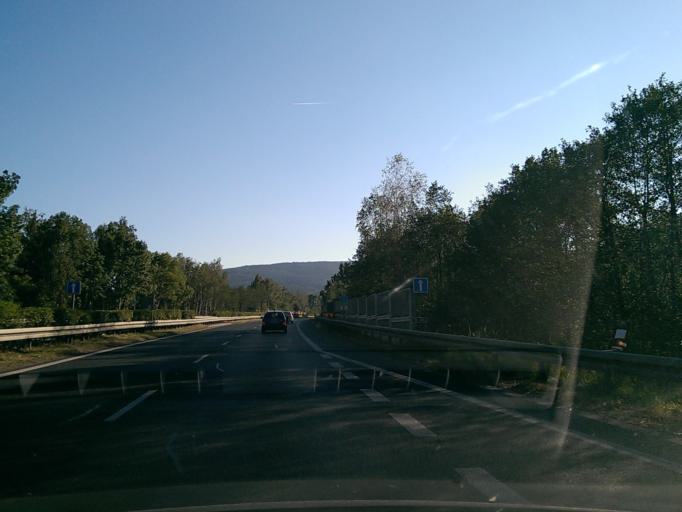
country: CZ
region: Liberecky
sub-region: Okres Liberec
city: Liberec
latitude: 50.7401
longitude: 15.0523
